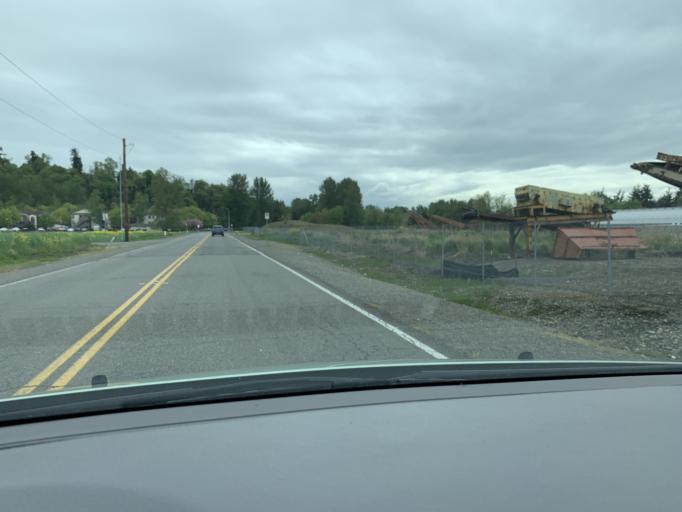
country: US
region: Washington
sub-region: King County
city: Kent
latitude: 47.3962
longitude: -122.2233
